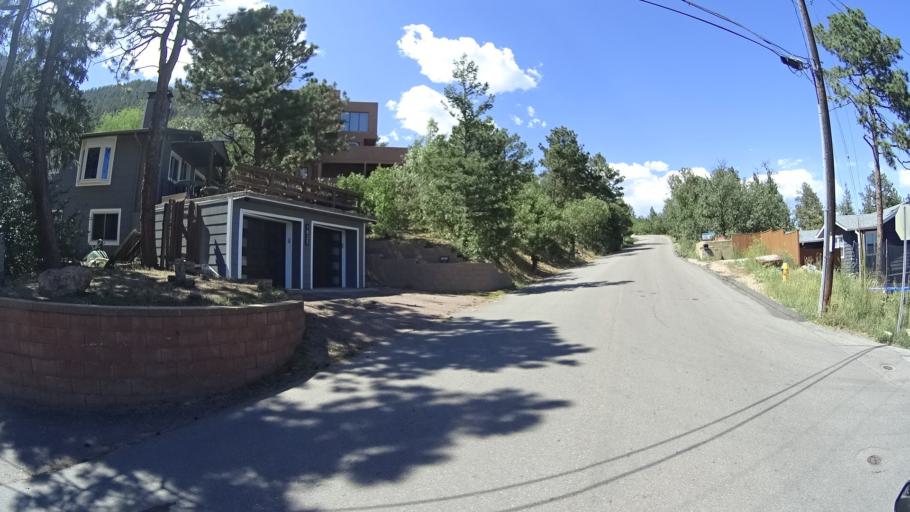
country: US
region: Colorado
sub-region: El Paso County
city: Colorado Springs
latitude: 38.7790
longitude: -104.8615
